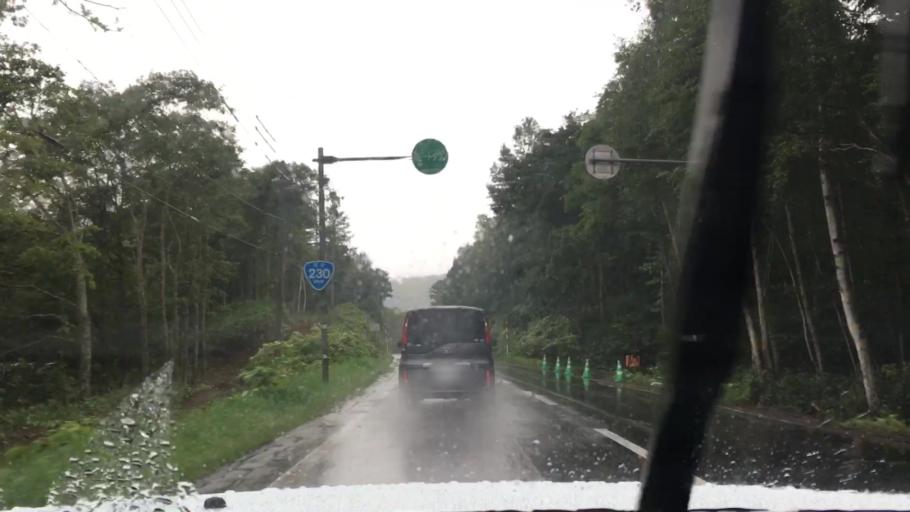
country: JP
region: Hokkaido
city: Otaru
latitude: 42.8477
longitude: 141.0244
